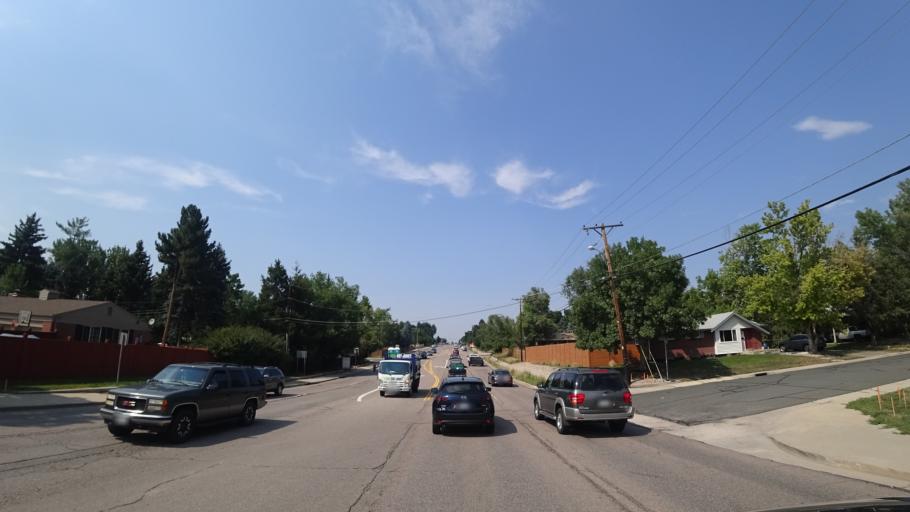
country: US
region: Colorado
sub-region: Arapahoe County
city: Greenwood Village
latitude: 39.6052
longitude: -104.9600
